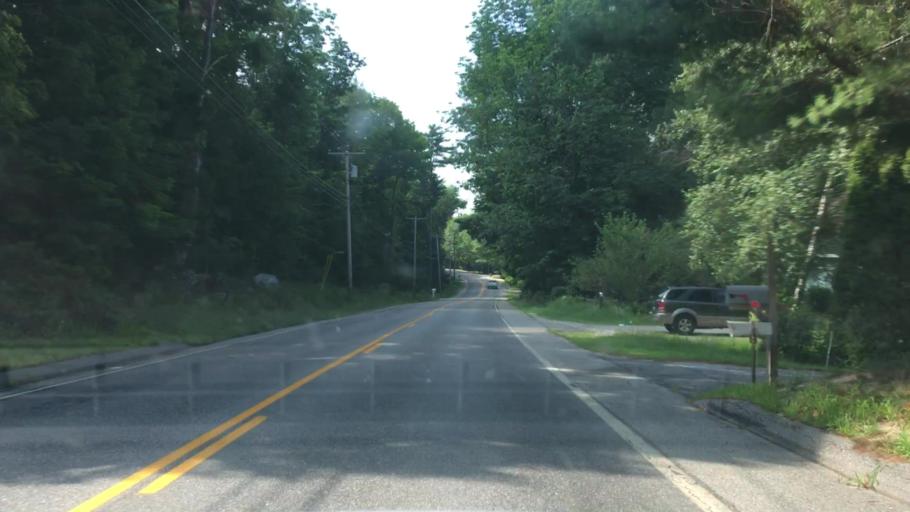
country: US
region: Maine
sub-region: Cumberland County
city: Raymond
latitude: 43.9083
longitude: -70.4409
